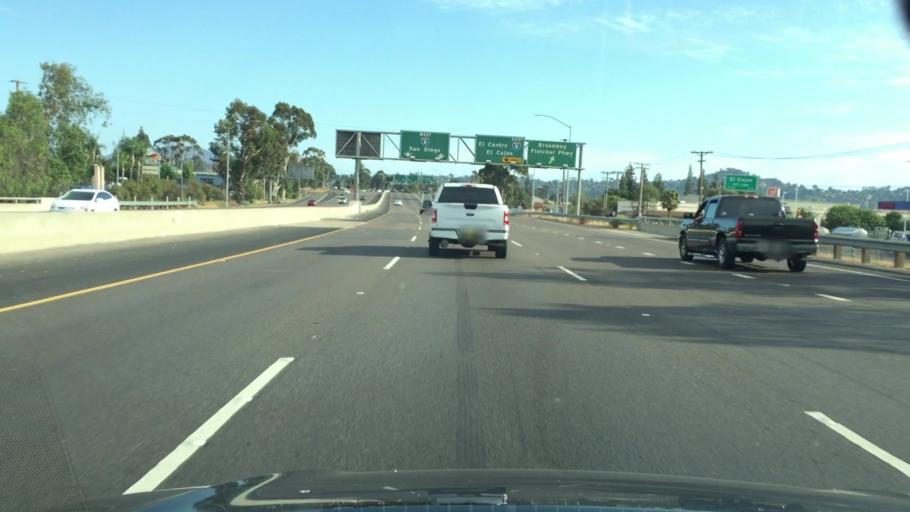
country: US
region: California
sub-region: San Diego County
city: El Cajon
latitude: 32.8128
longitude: -116.9619
